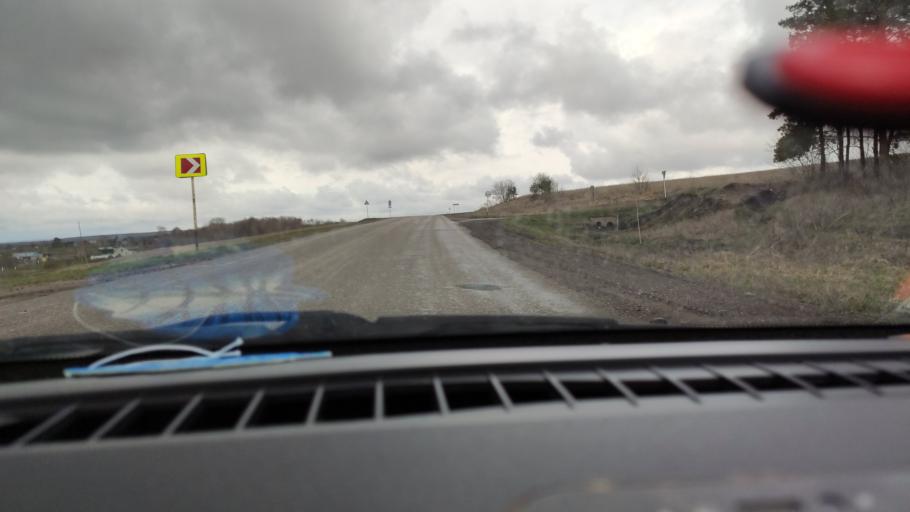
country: RU
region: Tatarstan
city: Nurlat
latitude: 54.3834
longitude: 50.7369
